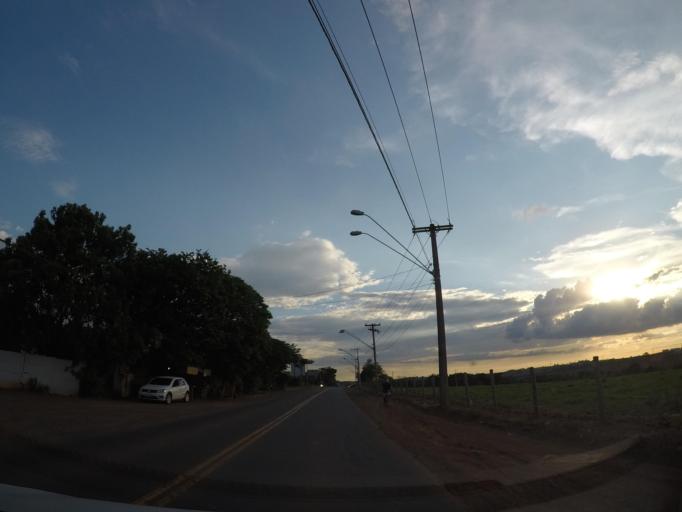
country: BR
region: Sao Paulo
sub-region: Sumare
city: Sumare
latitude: -22.8432
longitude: -47.2789
